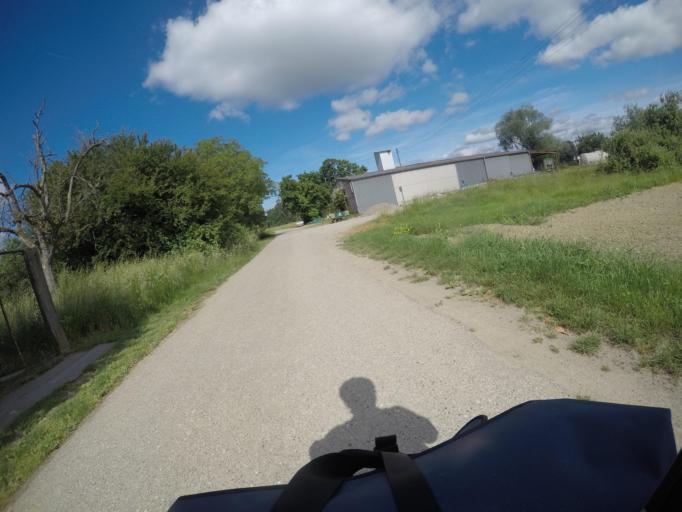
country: DE
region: Baden-Wuerttemberg
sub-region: Karlsruhe Region
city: Au am Rhein
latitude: 48.9384
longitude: 8.2035
